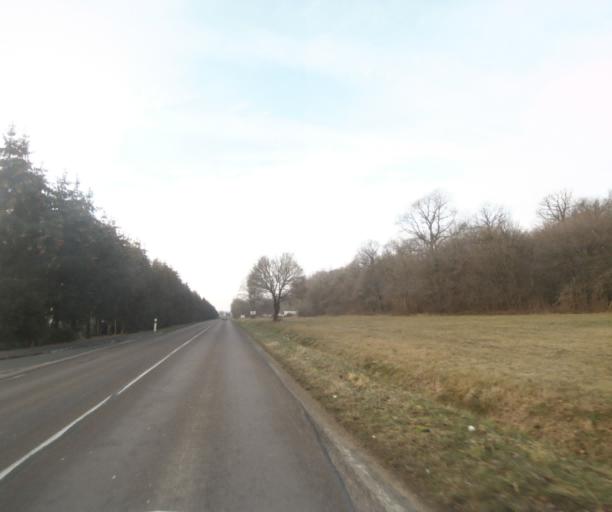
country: FR
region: Champagne-Ardenne
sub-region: Departement de la Haute-Marne
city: Bettancourt-la-Ferree
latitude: 48.6604
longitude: 4.9734
